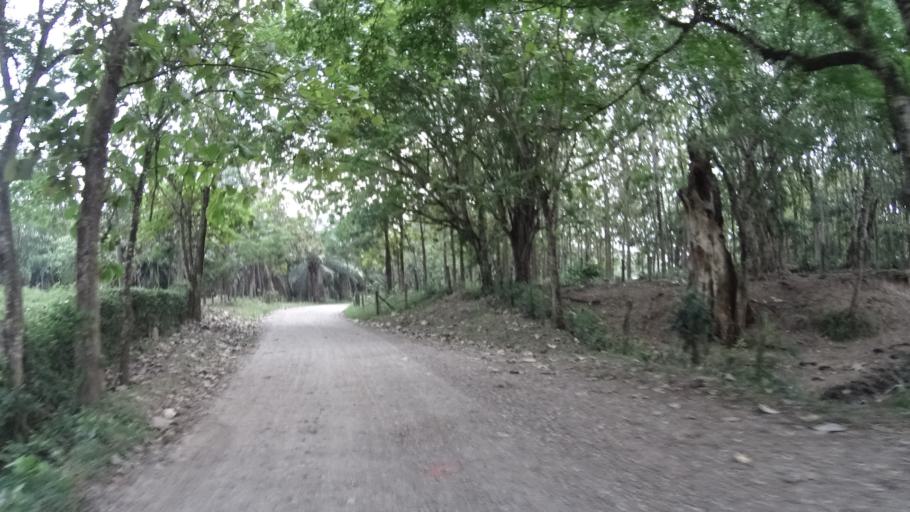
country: CO
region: Cundinamarca
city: Puerto Salgar
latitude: 5.4846
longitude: -74.6997
